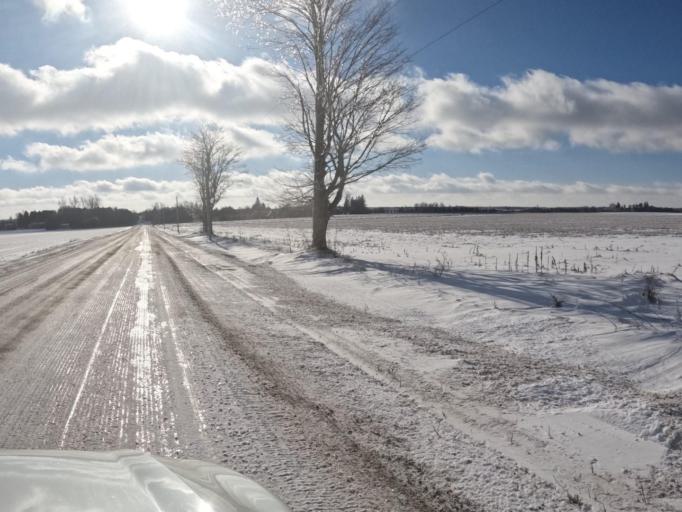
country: CA
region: Ontario
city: Shelburne
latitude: 43.9868
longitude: -80.4065
